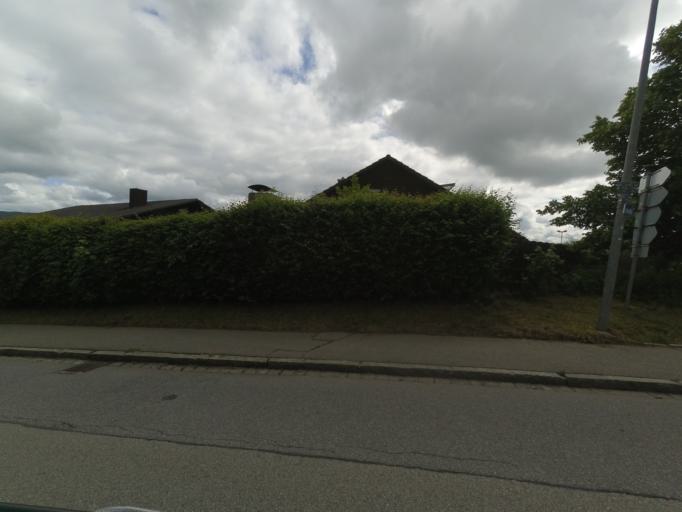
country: DE
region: Bavaria
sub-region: Lower Bavaria
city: Viechtach
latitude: 49.0708
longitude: 12.8902
